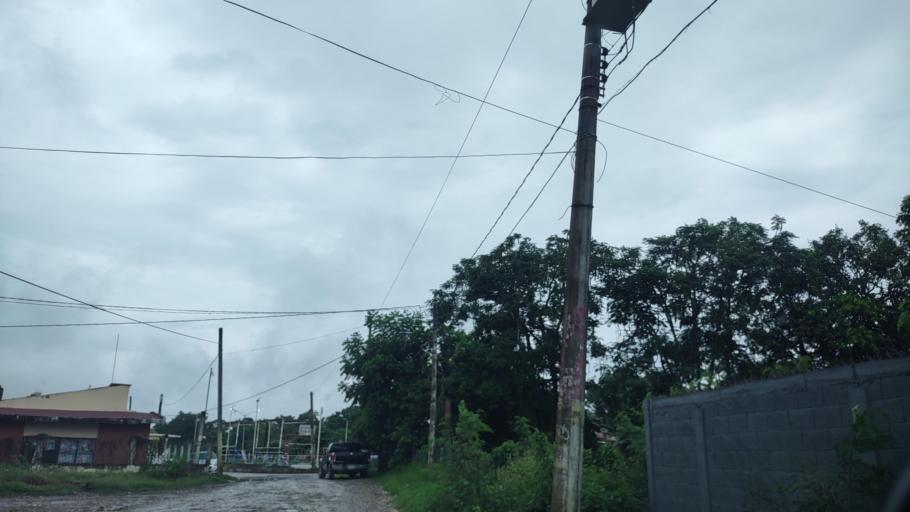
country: MX
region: San Luis Potosi
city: Tanquian de Escobedo
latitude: 21.5448
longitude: -98.5531
